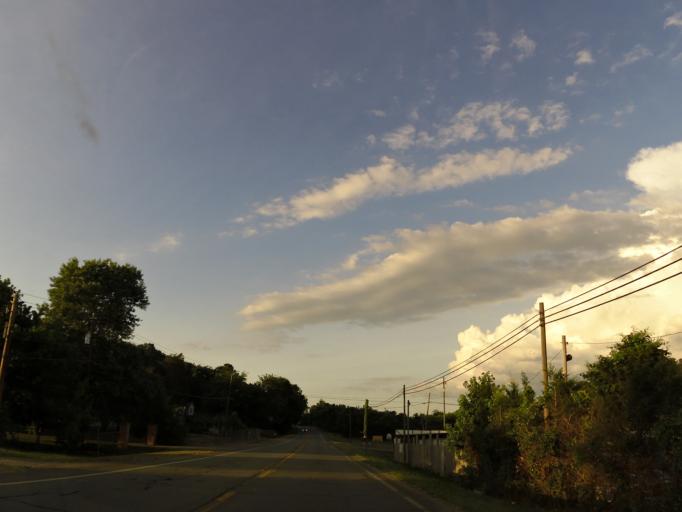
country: US
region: Georgia
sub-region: Dade County
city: Trenton
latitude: 34.9099
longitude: -85.4816
